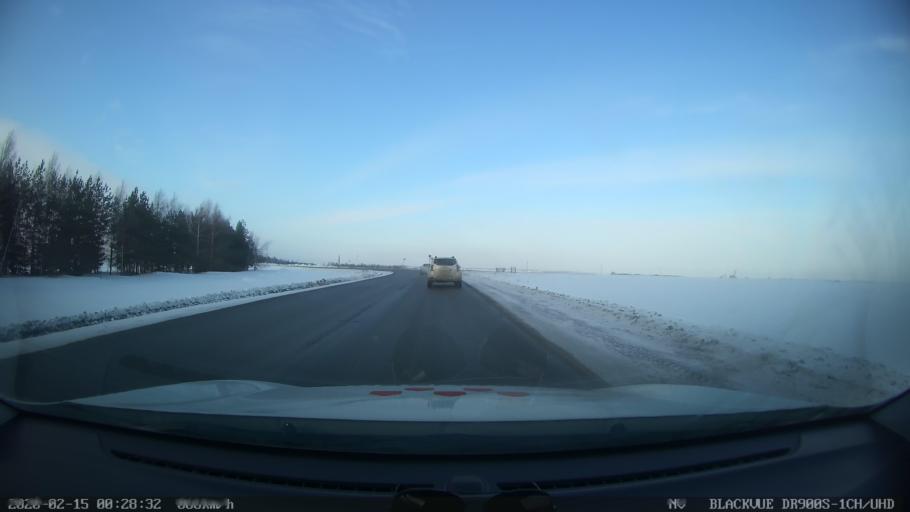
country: RU
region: Tatarstan
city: Verkhniy Uslon
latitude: 55.6432
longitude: 48.8761
